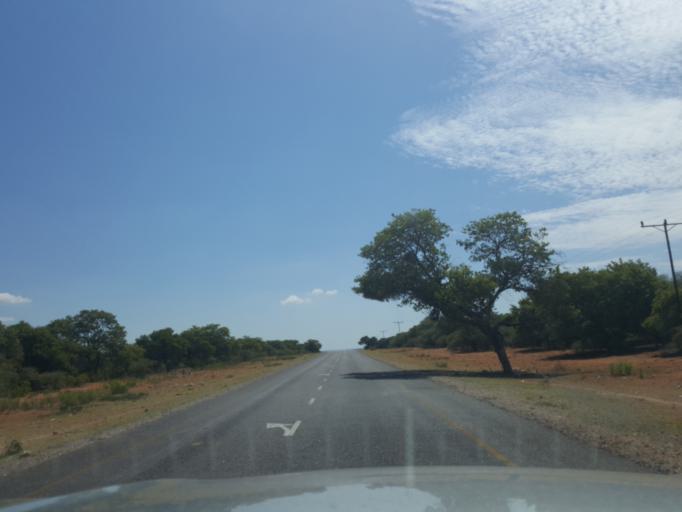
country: BW
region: Kweneng
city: Letlhakeng
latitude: -24.1228
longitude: 25.0912
